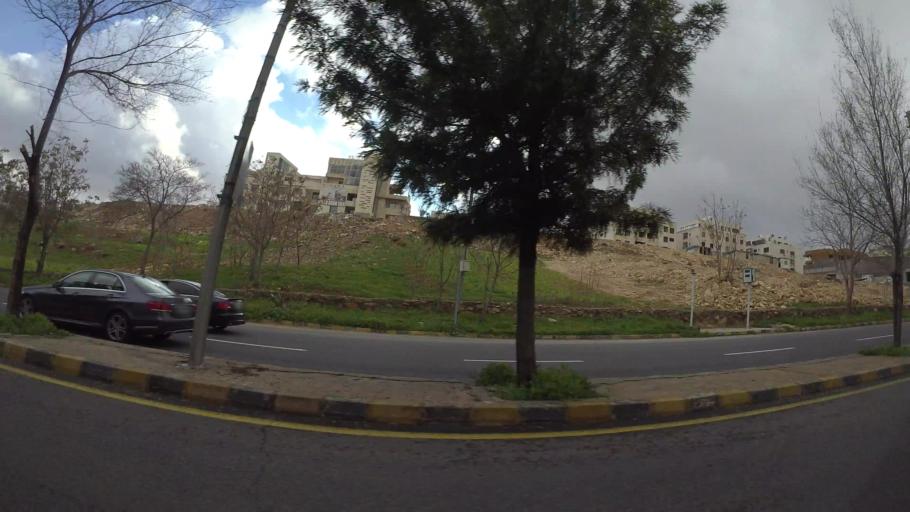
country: JO
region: Amman
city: Al Bunayyat ash Shamaliyah
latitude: 31.9455
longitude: 35.8886
